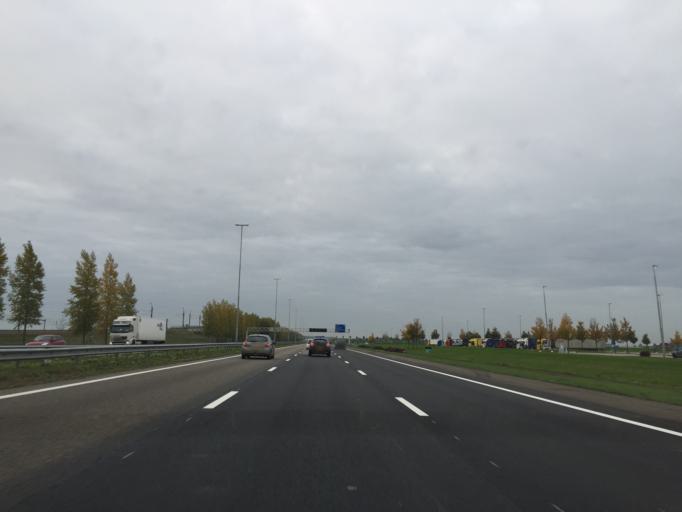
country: NL
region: North Brabant
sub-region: Gemeente Made en Drimmelen
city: Made
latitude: 51.6636
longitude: 4.6795
